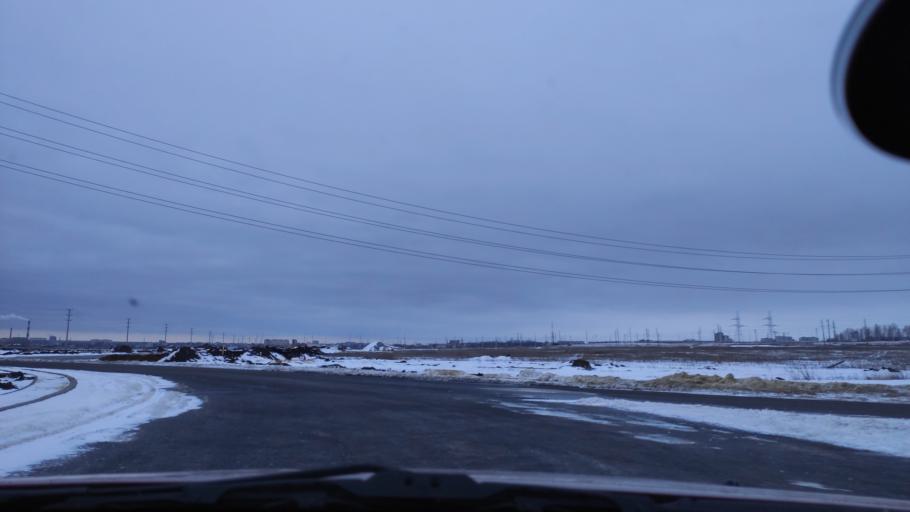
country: RU
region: Tambov
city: Donskoye
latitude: 52.7868
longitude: 41.4314
